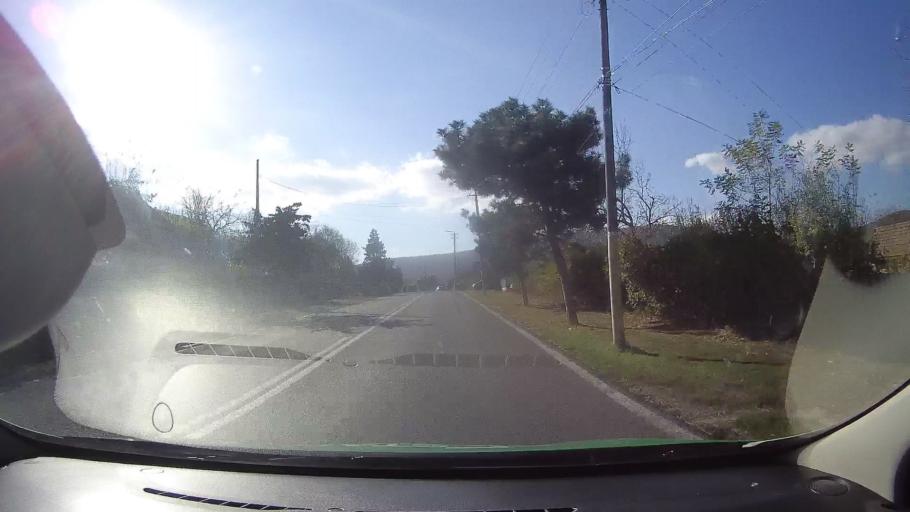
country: RO
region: Tulcea
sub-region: Oras Babadag
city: Babadag
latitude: 44.8797
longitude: 28.6926
